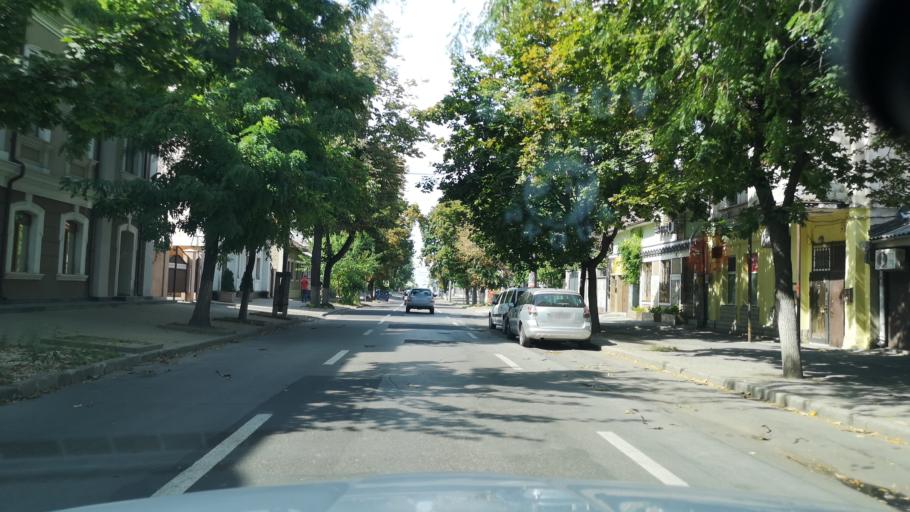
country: MD
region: Chisinau
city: Chisinau
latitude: 47.0249
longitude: 28.8204
